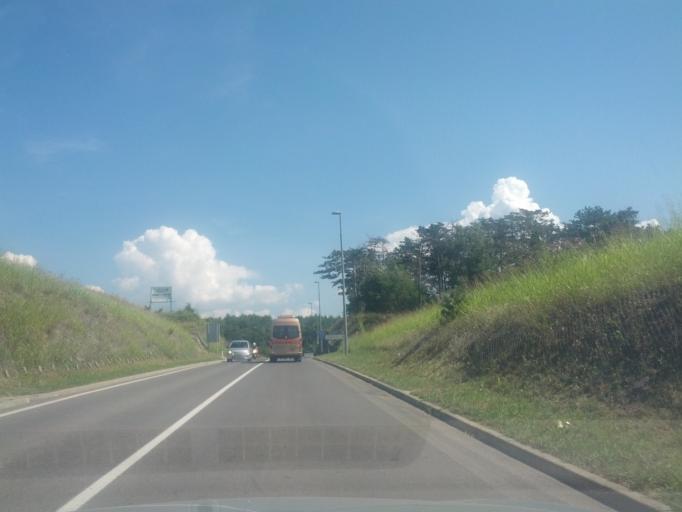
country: SI
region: Koper-Capodistria
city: Spodnje Skofije
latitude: 45.5681
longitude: 13.7815
